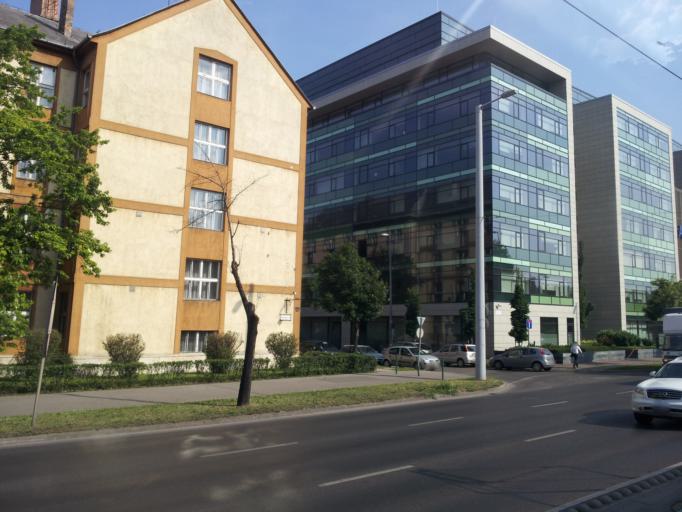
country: HU
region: Budapest
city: Budapest VIII. keruelet
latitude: 47.4788
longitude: 19.1010
